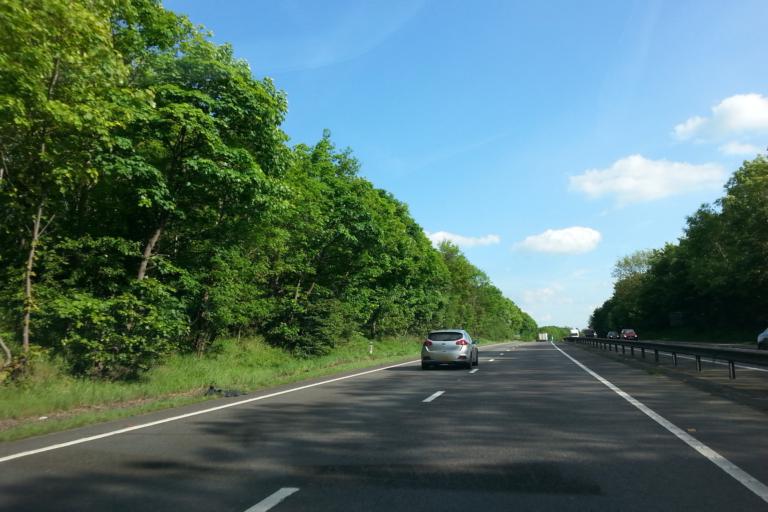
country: GB
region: England
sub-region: Nottinghamshire
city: Newark on Trent
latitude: 53.0829
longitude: -0.7746
